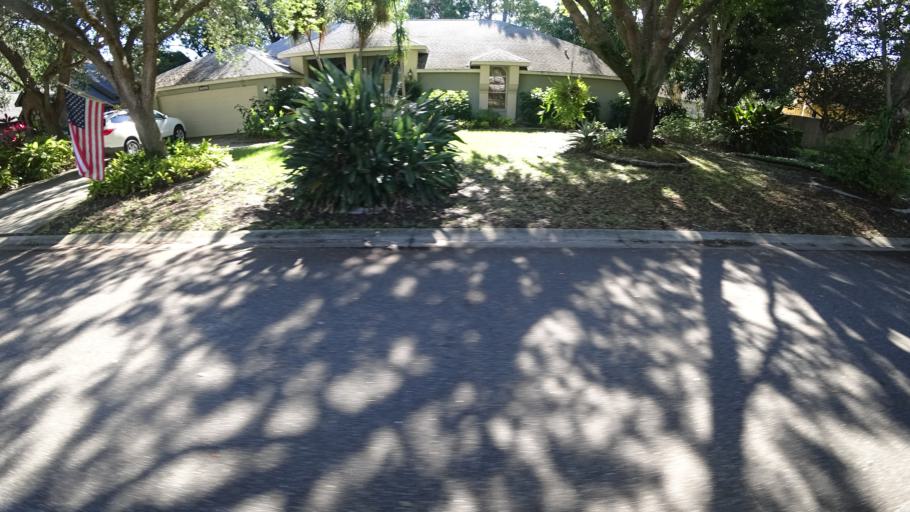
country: US
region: Florida
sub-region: Manatee County
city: West Bradenton
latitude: 27.5096
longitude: -82.6492
